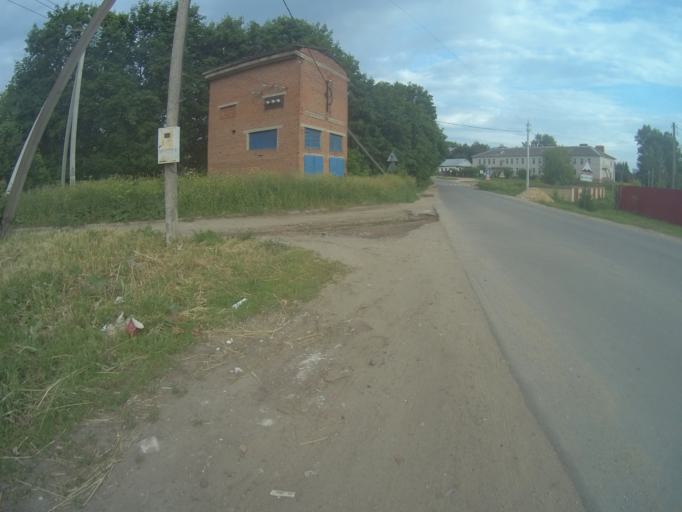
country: RU
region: Vladimir
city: Vladimir
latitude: 56.2223
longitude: 40.4056
